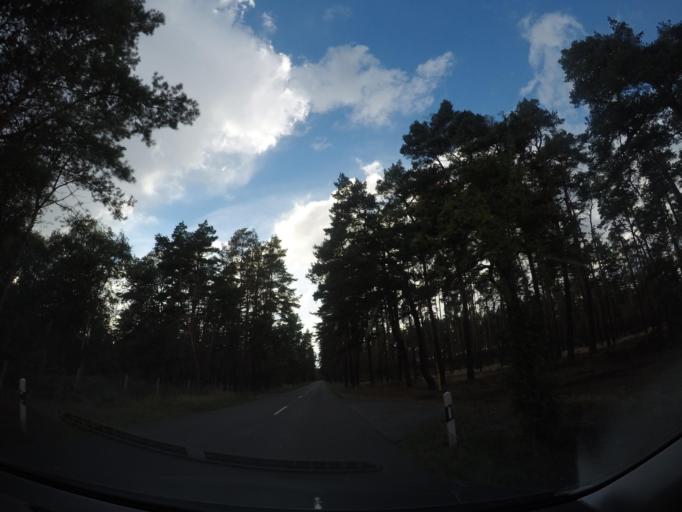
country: DE
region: Saxony-Anhalt
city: Calvorde
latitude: 52.4580
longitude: 11.2869
